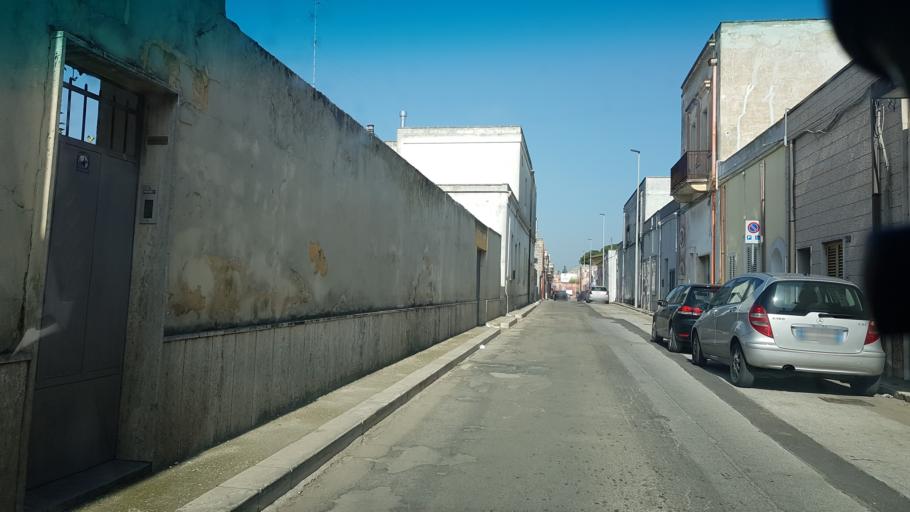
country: IT
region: Apulia
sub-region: Provincia di Brindisi
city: San Pietro Vernotico
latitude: 40.4857
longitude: 18.0012
